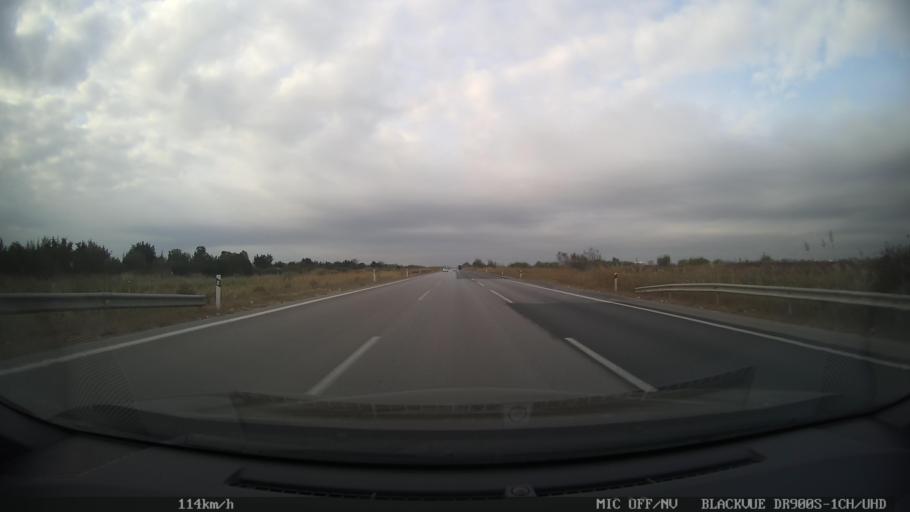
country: GR
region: Central Macedonia
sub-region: Nomos Thessalonikis
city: Chalastra
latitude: 40.6322
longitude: 22.7779
